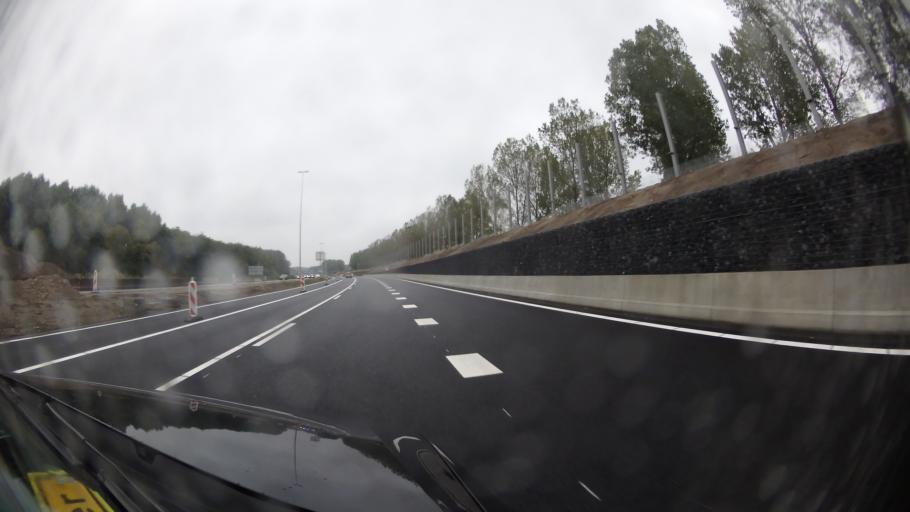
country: NL
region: Flevoland
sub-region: Gemeente Almere
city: Almere Stad
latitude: 52.3526
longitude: 5.1739
